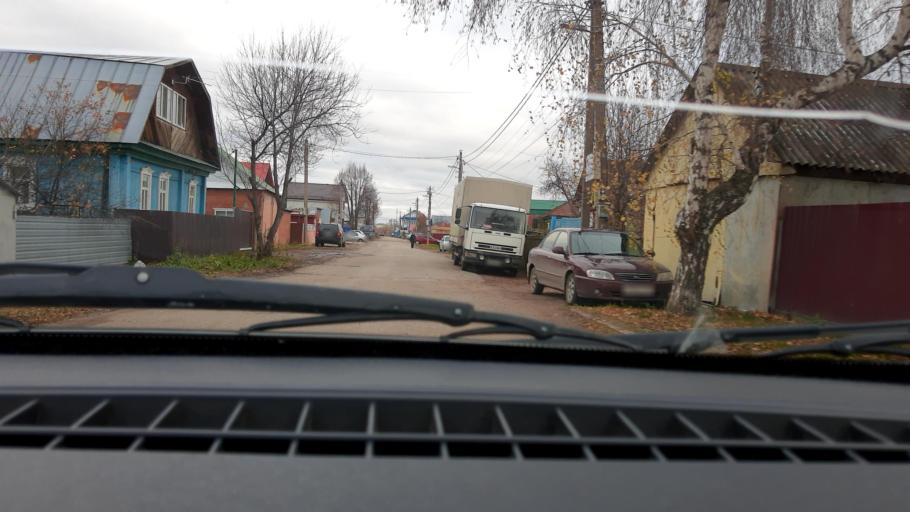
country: RU
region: Bashkortostan
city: Ufa
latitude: 54.7390
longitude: 55.9075
